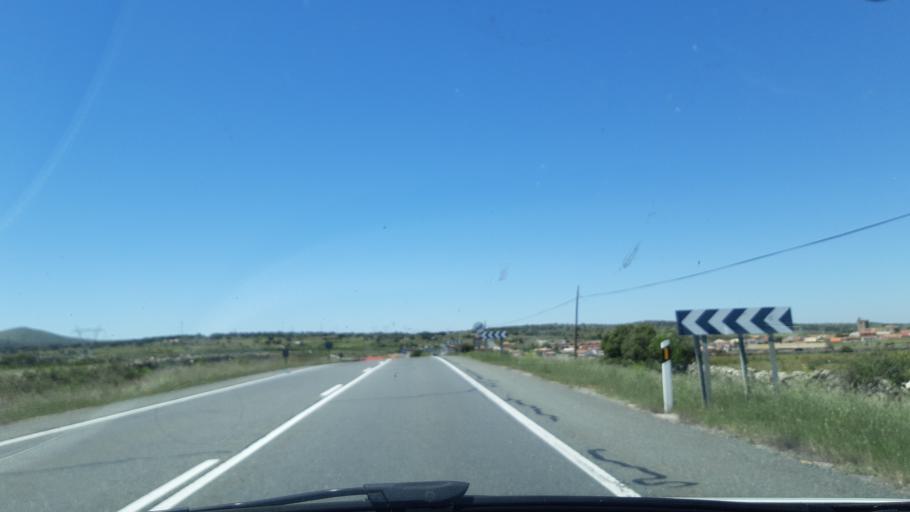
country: ES
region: Castille and Leon
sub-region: Provincia de Segovia
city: Zarzuela del Monte
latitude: 40.7550
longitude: -4.3211
